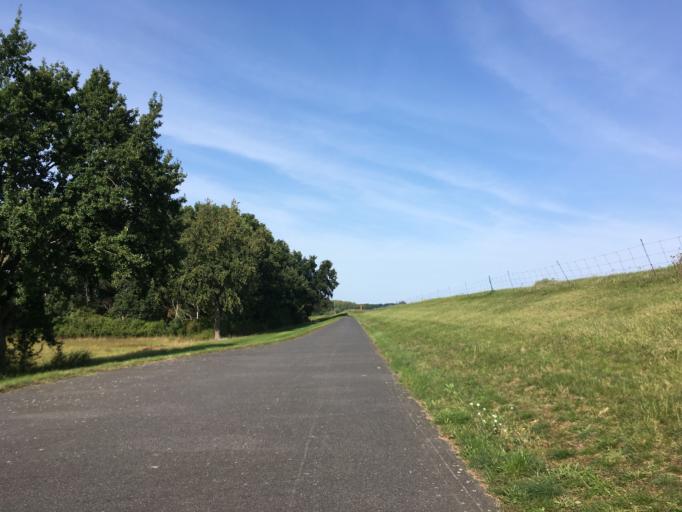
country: DE
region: Brandenburg
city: Vogelsang
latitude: 52.2106
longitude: 14.6992
